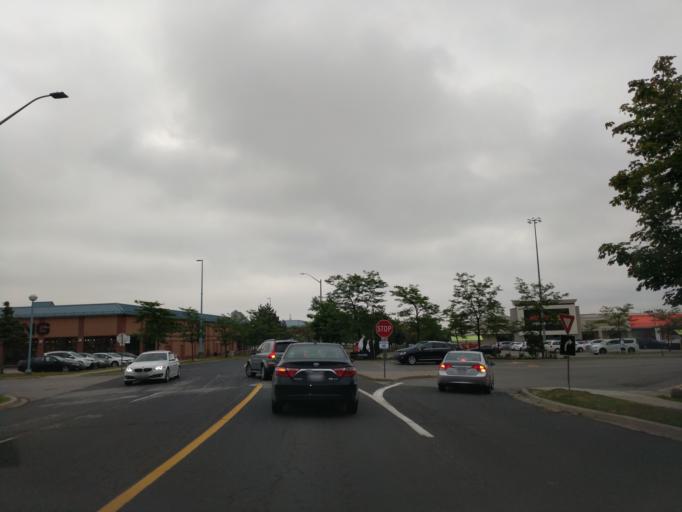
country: CA
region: Ontario
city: Markham
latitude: 43.8498
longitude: -79.3513
